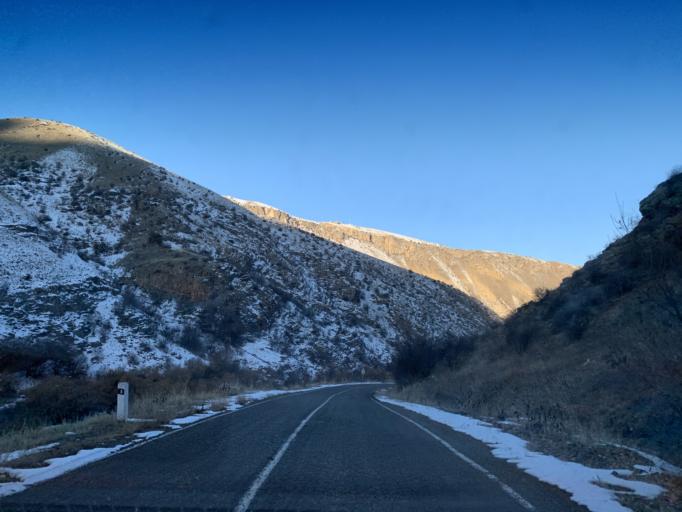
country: AM
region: Vayots' Dzori Marz
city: Areni
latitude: 39.6909
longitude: 45.2194
